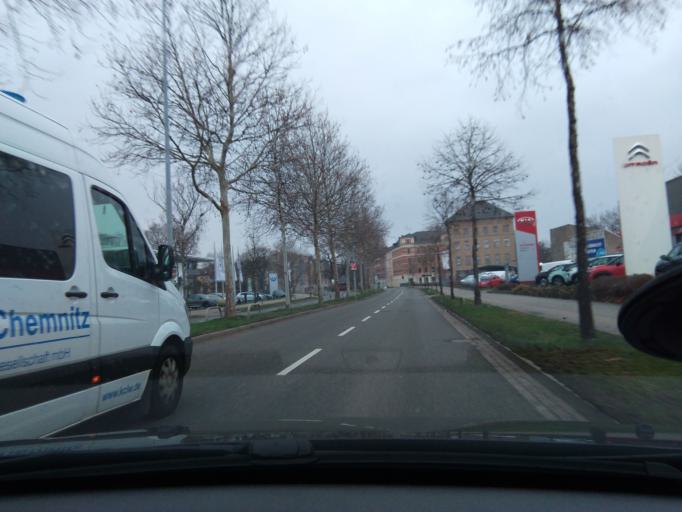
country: DE
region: Saxony
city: Chemnitz
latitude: 50.8451
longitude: 12.9199
